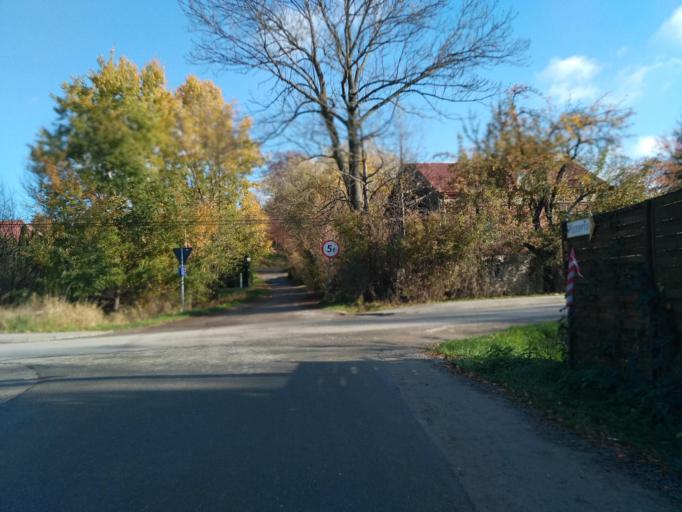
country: PL
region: Subcarpathian Voivodeship
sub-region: Powiat rzeszowski
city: Niechobrz
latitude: 50.0125
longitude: 21.8969
